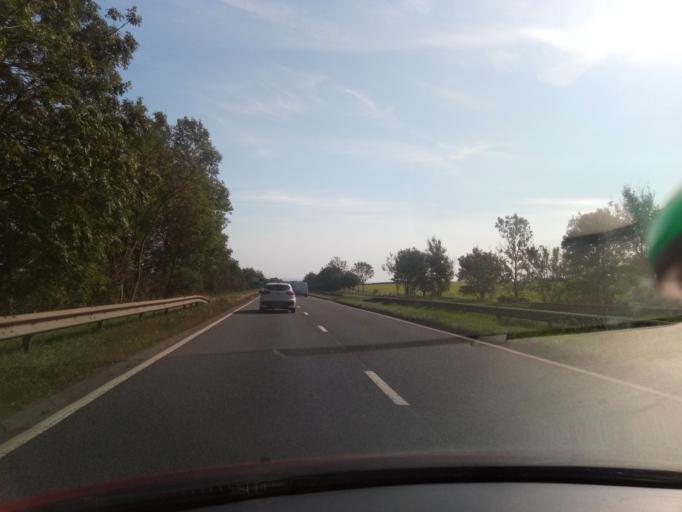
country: GB
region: England
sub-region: Sunderland
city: Ryhope
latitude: 54.8494
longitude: -1.3881
